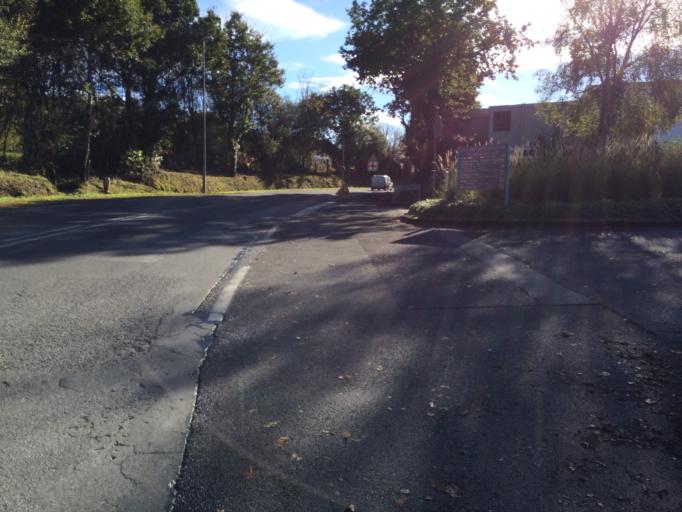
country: FR
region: Brittany
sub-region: Departement du Finistere
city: Pencran
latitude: 48.4490
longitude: -4.2338
